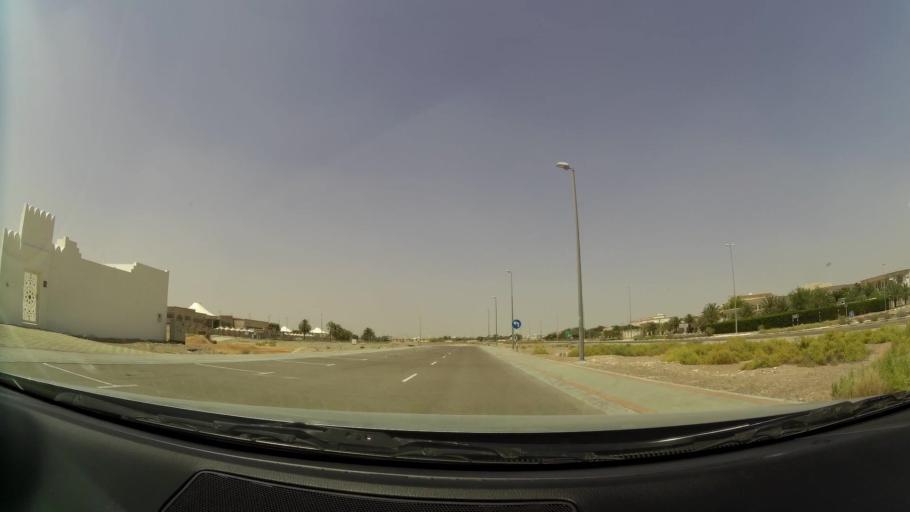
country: AE
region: Abu Dhabi
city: Al Ain
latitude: 24.2540
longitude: 55.6889
